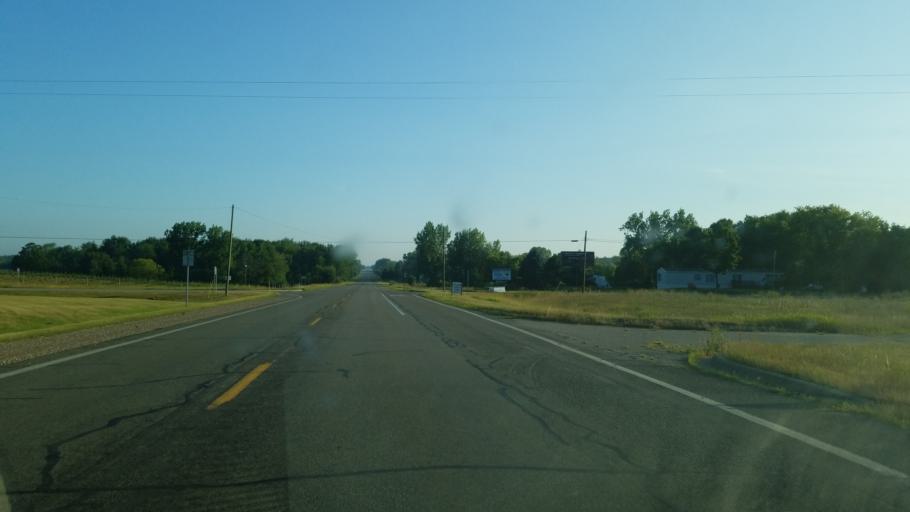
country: US
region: Michigan
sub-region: Montcalm County
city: Stanton
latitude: 43.3569
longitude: -85.0852
